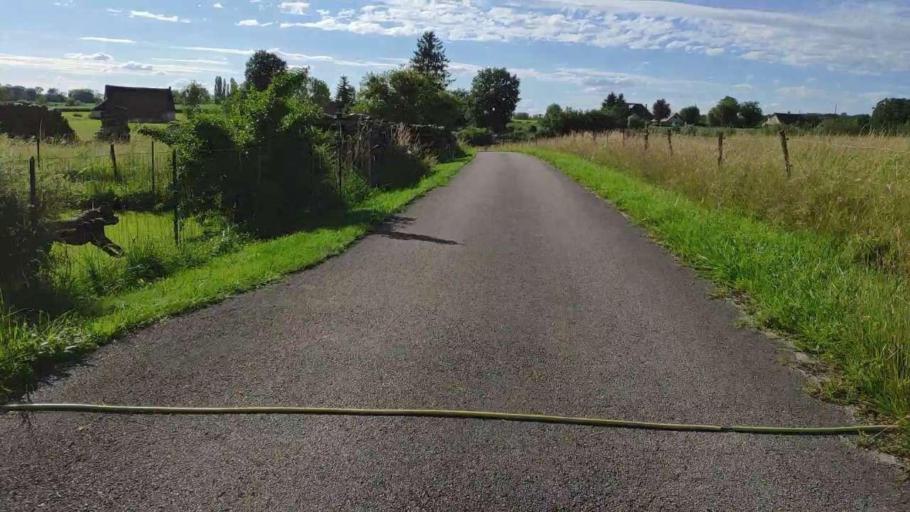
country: FR
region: Franche-Comte
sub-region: Departement du Jura
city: Bletterans
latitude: 46.8243
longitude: 5.4952
